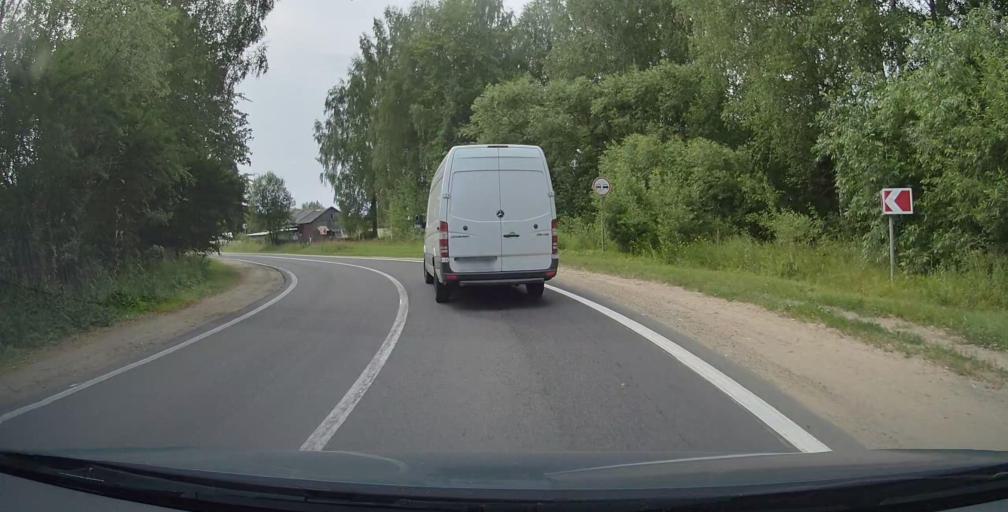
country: RU
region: Jaroslavl
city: Rybinsk
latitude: 57.9774
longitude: 38.7405
